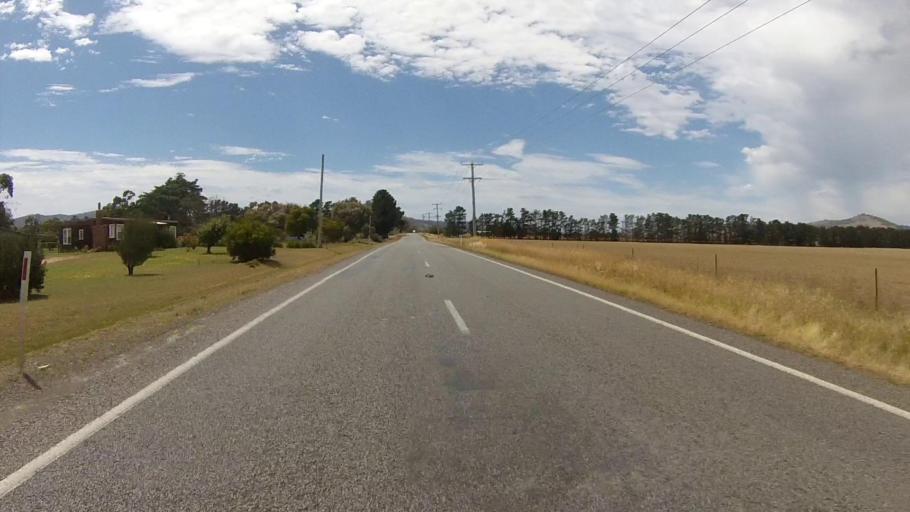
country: AU
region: Tasmania
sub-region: Clarence
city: Cambridge
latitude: -42.6886
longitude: 147.4423
